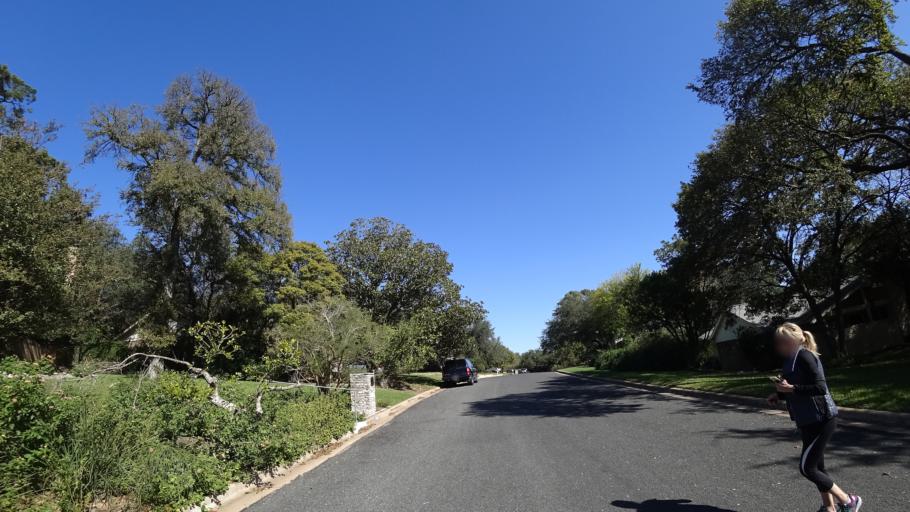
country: US
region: Texas
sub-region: Williamson County
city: Jollyville
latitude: 30.3777
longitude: -97.7474
